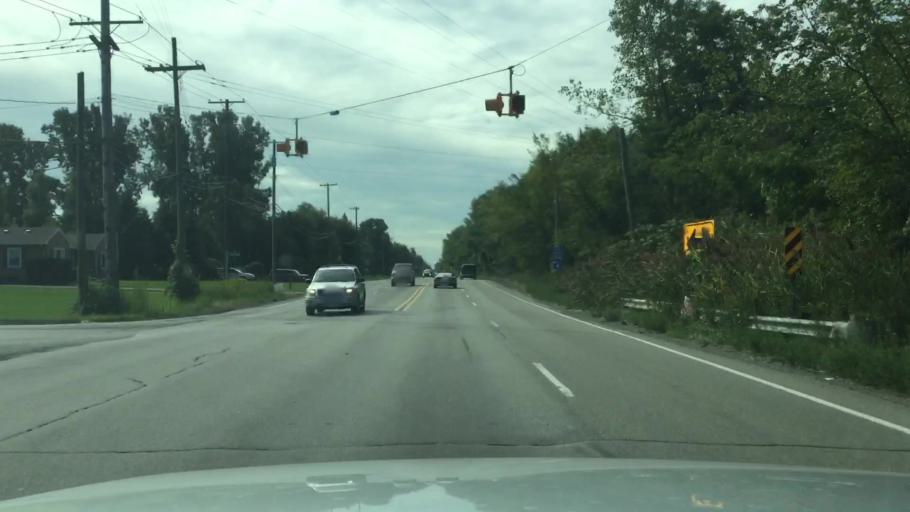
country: US
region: Michigan
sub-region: Wayne County
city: Canton
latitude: 42.2587
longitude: -83.4867
